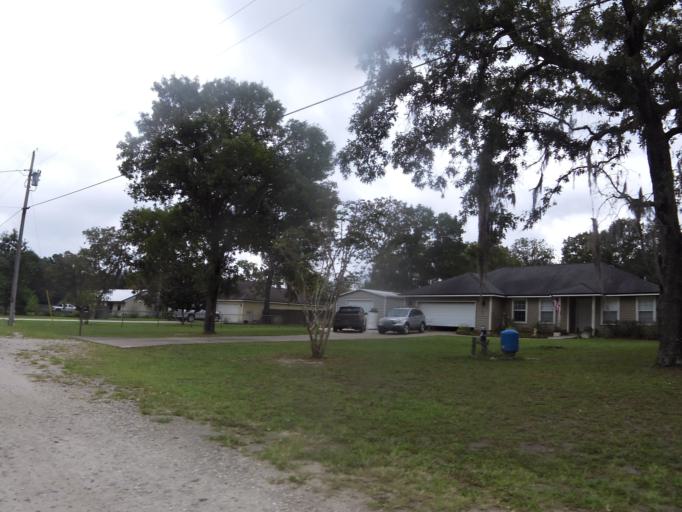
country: US
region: Florida
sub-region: Clay County
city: Middleburg
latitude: 30.1068
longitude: -81.9581
